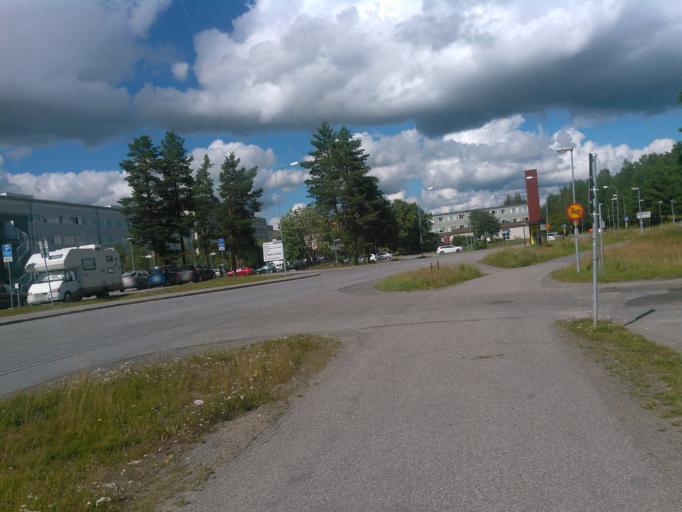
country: SE
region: Vaesterbotten
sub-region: Umea Kommun
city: Umea
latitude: 63.8148
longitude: 20.3032
